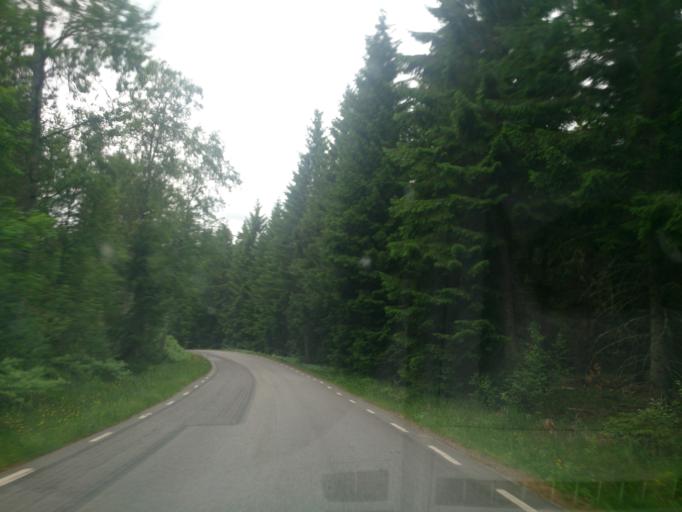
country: SE
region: OEstergoetland
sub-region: Soderkopings Kommun
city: Soederkoeping
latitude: 58.3106
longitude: 16.2915
